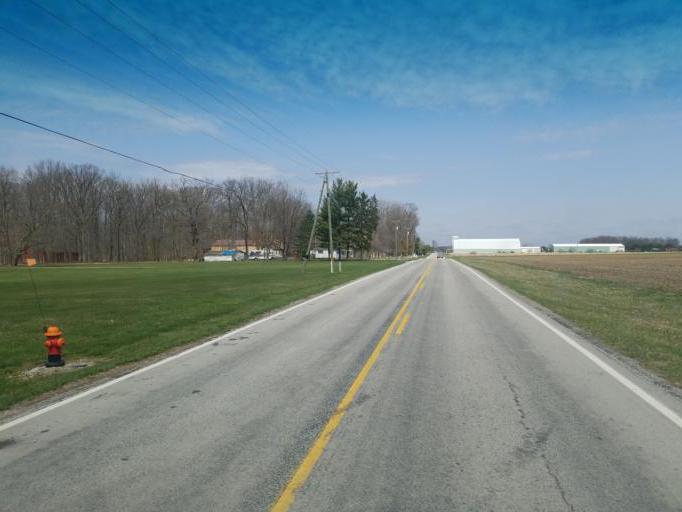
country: US
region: Ohio
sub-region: Wyandot County
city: Upper Sandusky
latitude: 40.8389
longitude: -83.2560
